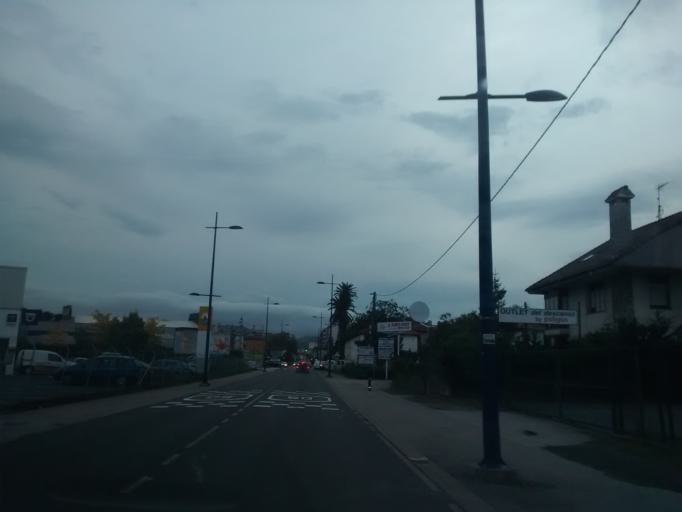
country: ES
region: Cantabria
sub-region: Provincia de Cantabria
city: Colindres
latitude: 43.3988
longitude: -3.4420
